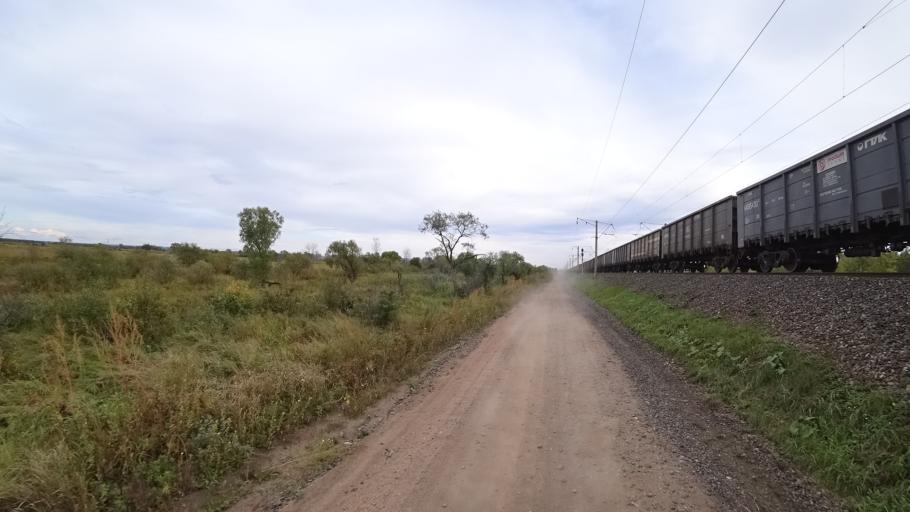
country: RU
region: Amur
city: Arkhara
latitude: 49.3582
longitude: 130.1520
